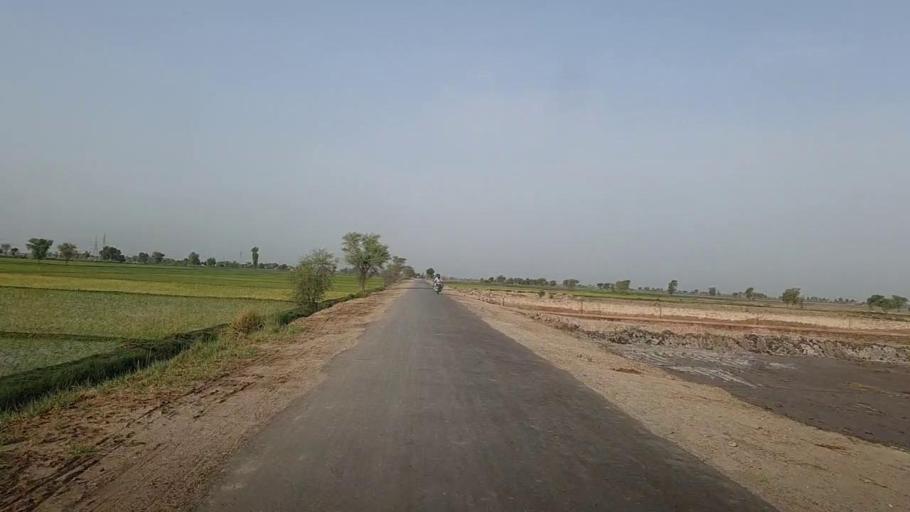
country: PK
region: Sindh
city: Mehar
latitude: 27.1620
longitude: 67.8114
